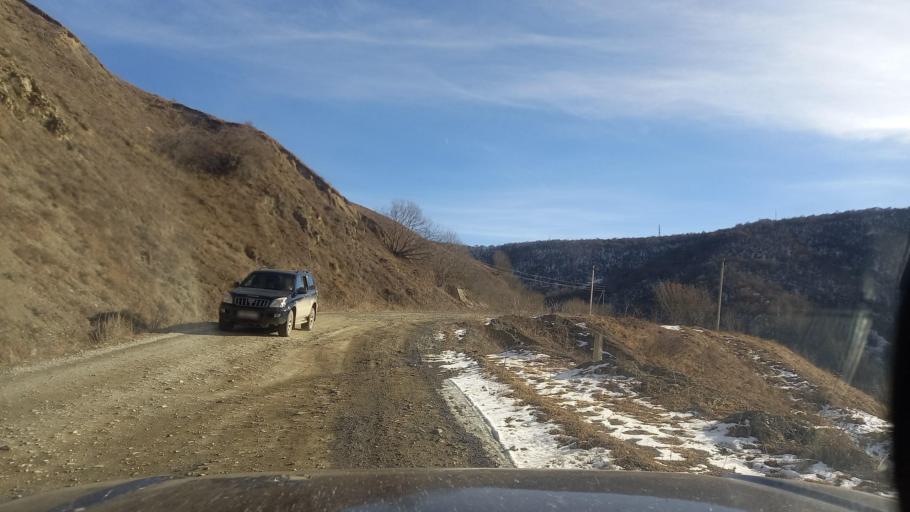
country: RU
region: North Ossetia
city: Verkhniy Fiagdon
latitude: 42.8380
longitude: 44.4664
